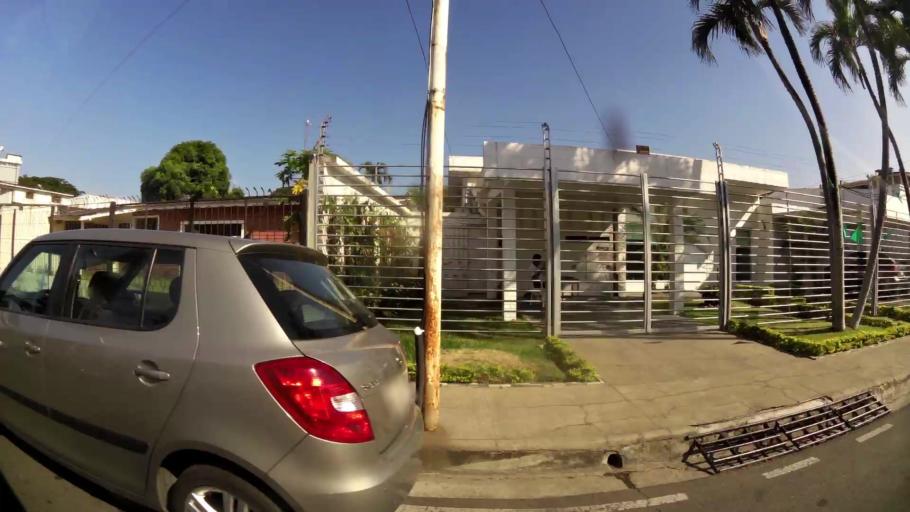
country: EC
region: Guayas
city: Guayaquil
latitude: -2.1744
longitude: -79.9048
